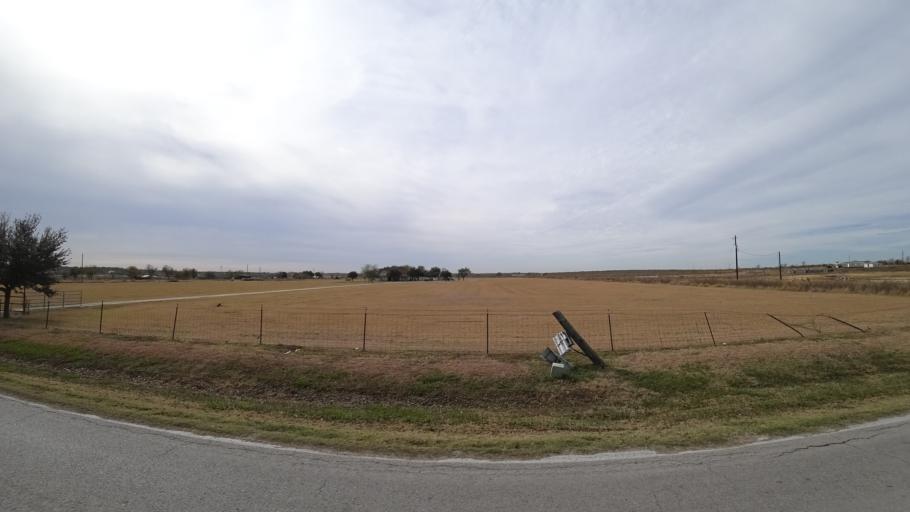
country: US
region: Texas
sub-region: Travis County
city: Garfield
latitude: 30.1222
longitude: -97.5969
